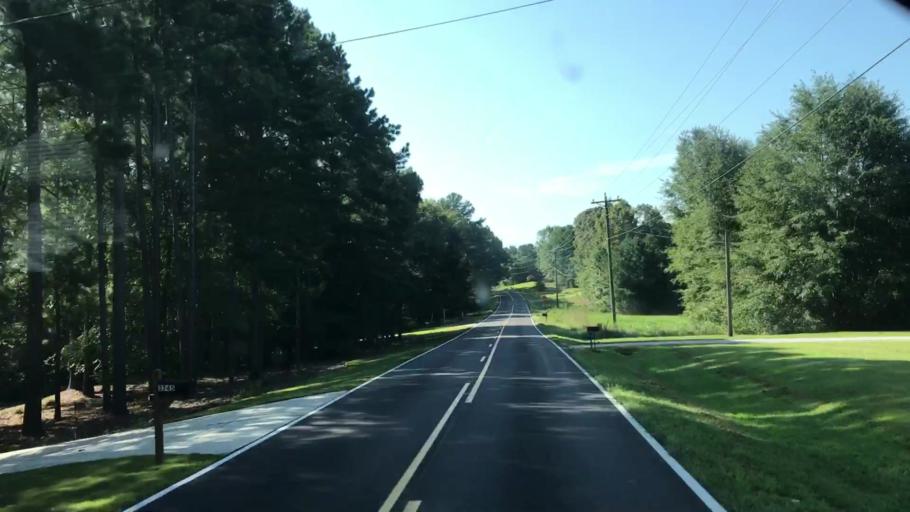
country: US
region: Georgia
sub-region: Walton County
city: Loganville
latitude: 33.8652
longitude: -83.7988
